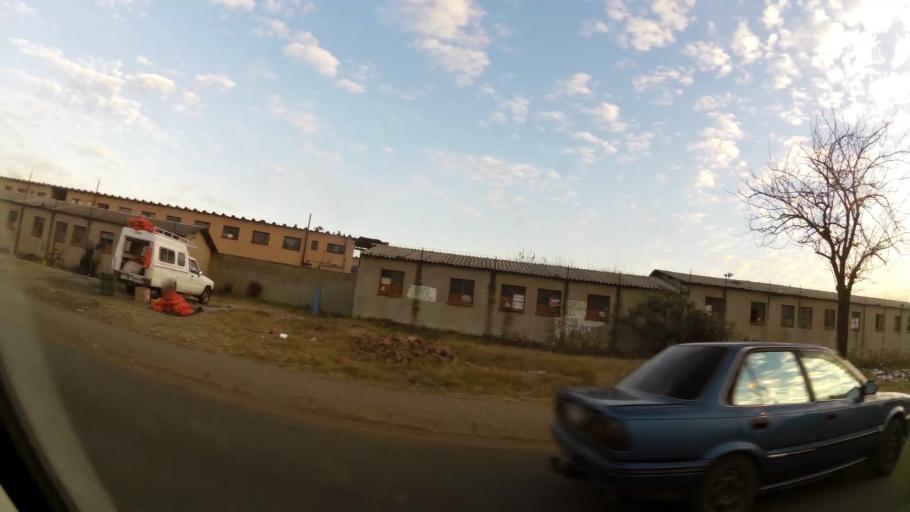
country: ZA
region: Gauteng
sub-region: City of Tshwane Metropolitan Municipality
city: Pretoria
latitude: -25.7148
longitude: 28.3404
